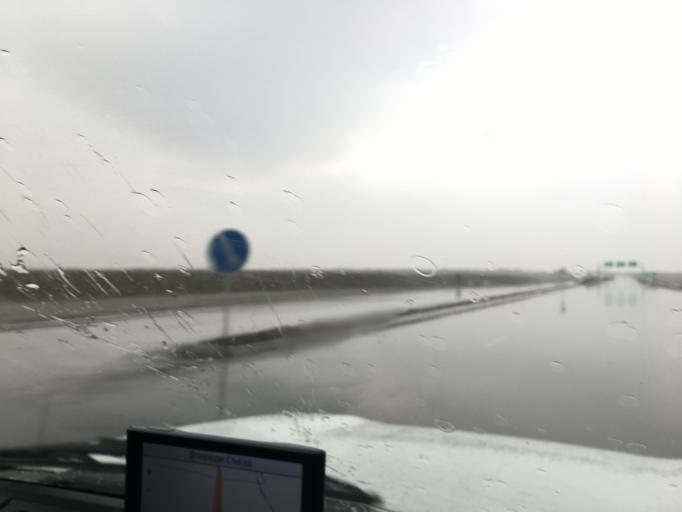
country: TM
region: Ahal
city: Annau
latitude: 37.8431
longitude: 58.7178
